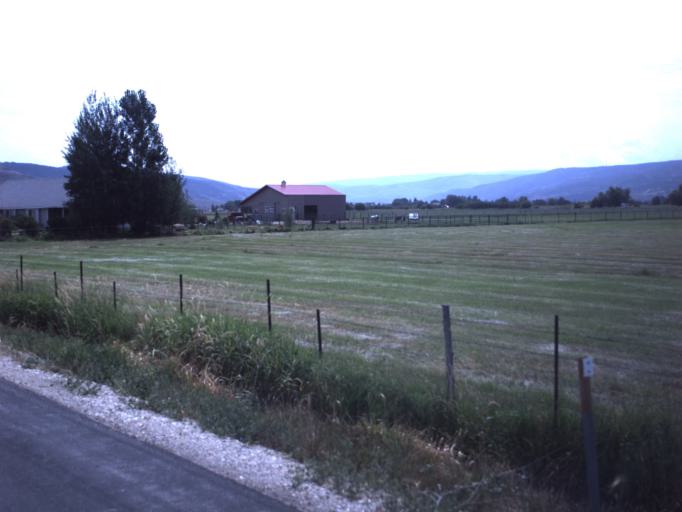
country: US
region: Utah
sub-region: Summit County
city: Francis
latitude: 40.6105
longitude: -111.2744
